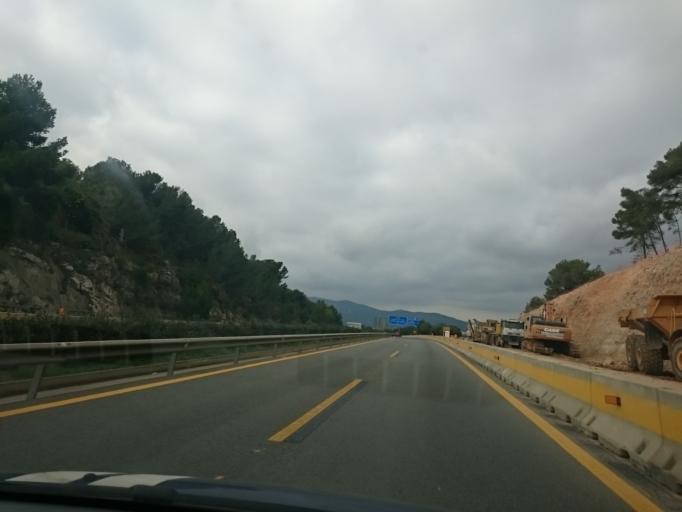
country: ES
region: Catalonia
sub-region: Provincia de Barcelona
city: Sitges
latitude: 41.2506
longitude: 1.8026
